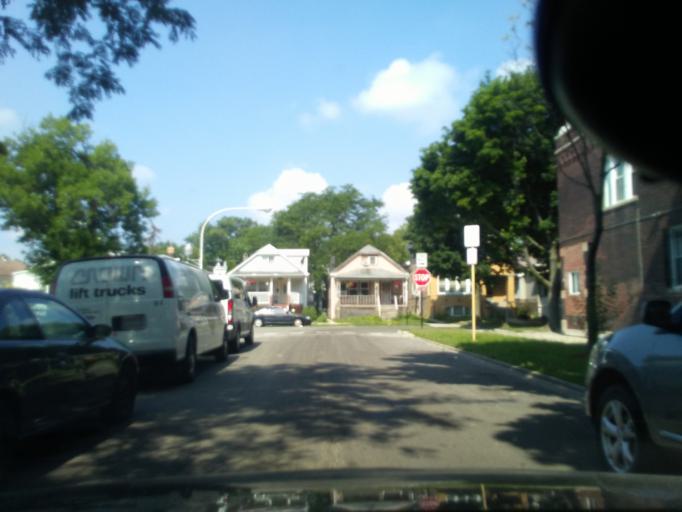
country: US
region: Illinois
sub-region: Cook County
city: Oak Park
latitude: 41.9197
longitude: -87.7482
